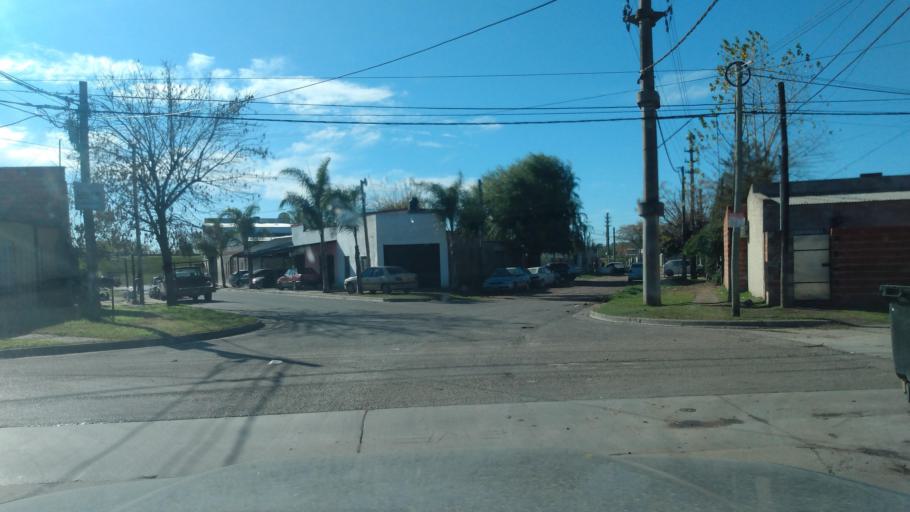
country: AR
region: Buenos Aires
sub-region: Partido de Lujan
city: Lujan
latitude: -34.5632
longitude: -59.0889
